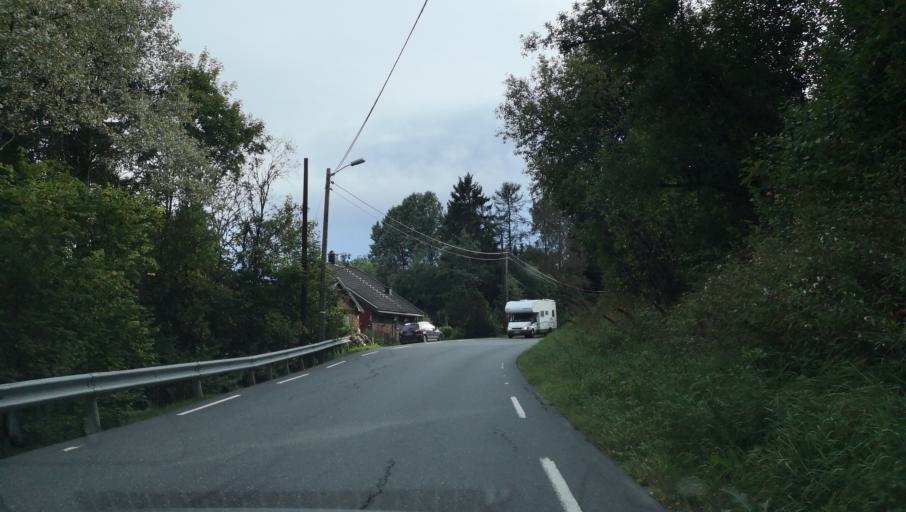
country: NO
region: Ostfold
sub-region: Hobol
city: Tomter
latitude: 59.6624
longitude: 11.0036
